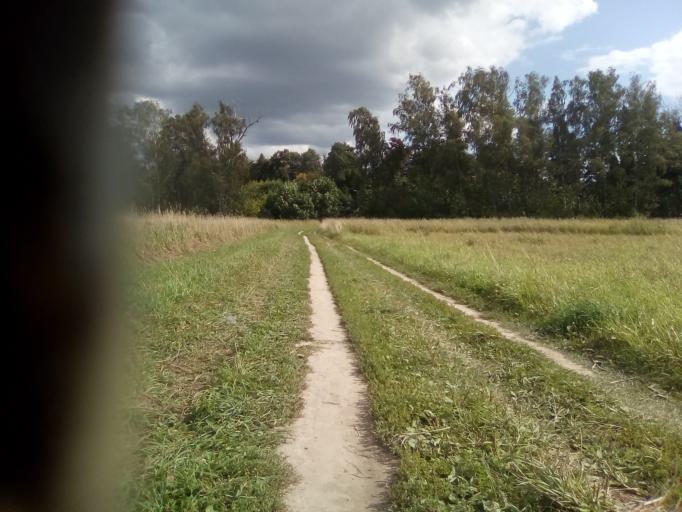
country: RU
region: Moskovskaya
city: Zhavoronki
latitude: 55.6500
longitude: 37.1467
